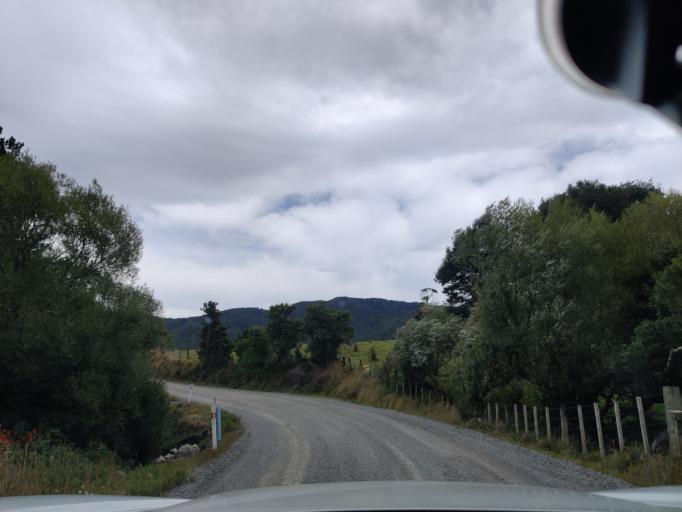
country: NZ
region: Wellington
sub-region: Masterton District
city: Masterton
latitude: -41.0414
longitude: 175.4083
